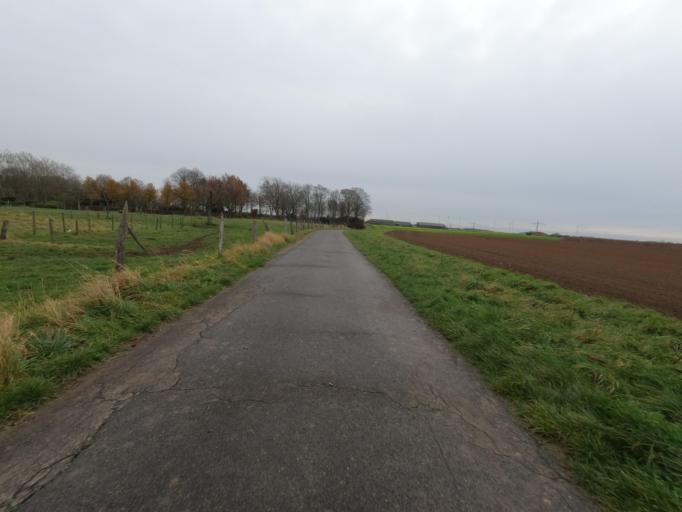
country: DE
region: North Rhine-Westphalia
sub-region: Regierungsbezirk Koln
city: Heinsberg
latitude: 51.0462
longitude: 6.1219
